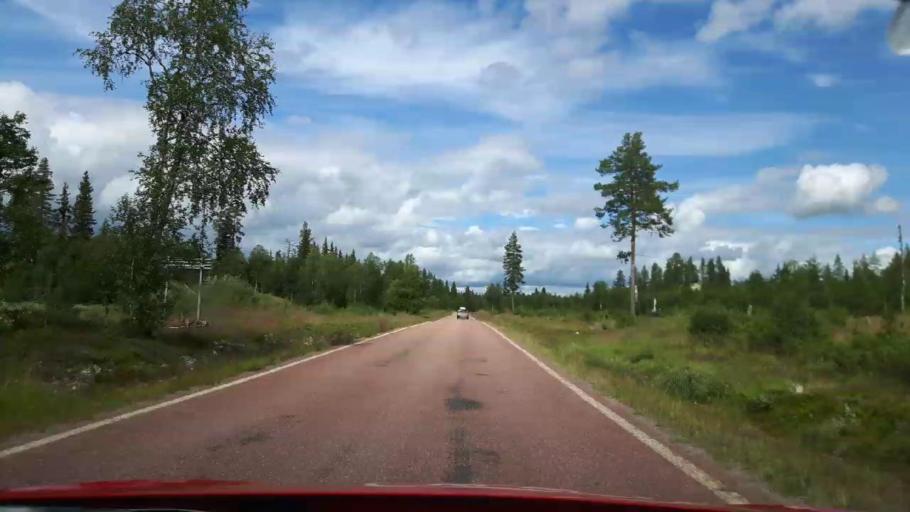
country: NO
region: Hedmark
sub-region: Trysil
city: Innbygda
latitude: 62.0041
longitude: 12.9764
